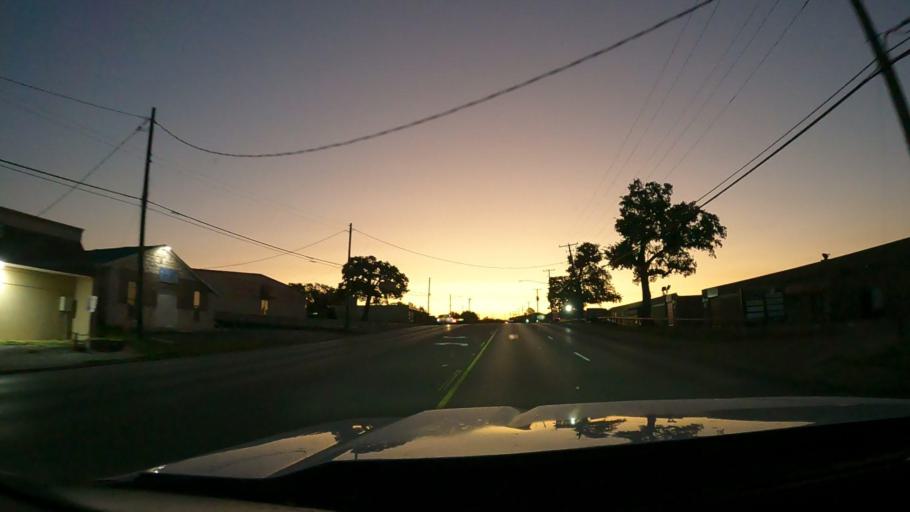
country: US
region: Texas
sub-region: Tarrant County
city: Pantego
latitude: 32.7358
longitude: -97.1380
